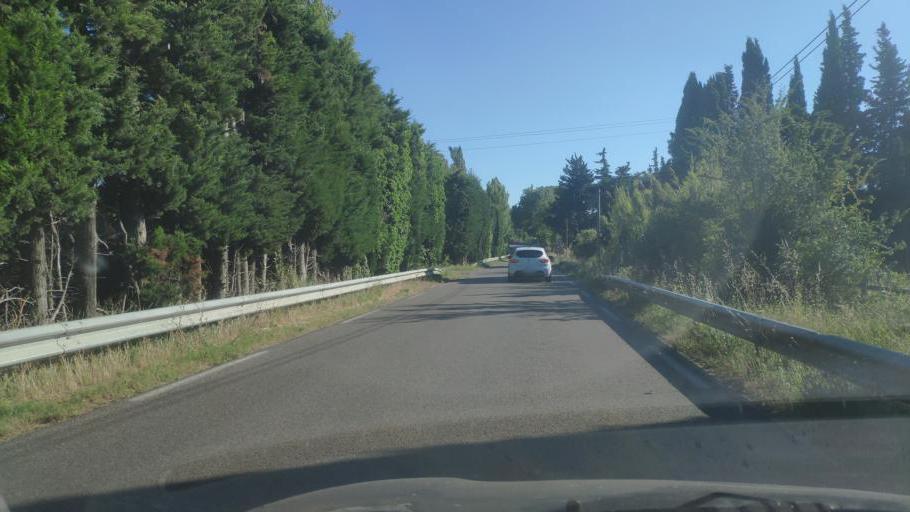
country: FR
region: Provence-Alpes-Cote d'Azur
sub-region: Departement du Vaucluse
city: Aubignan
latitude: 44.0891
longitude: 5.0220
